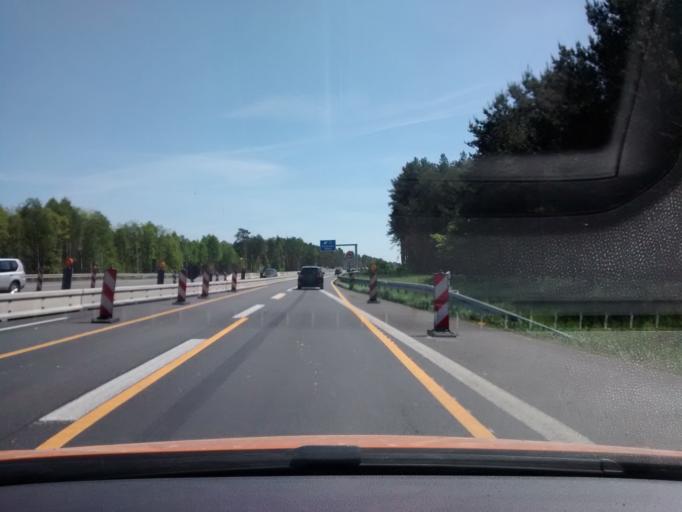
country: DE
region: Brandenburg
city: Erkner
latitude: 52.3231
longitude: 13.7621
